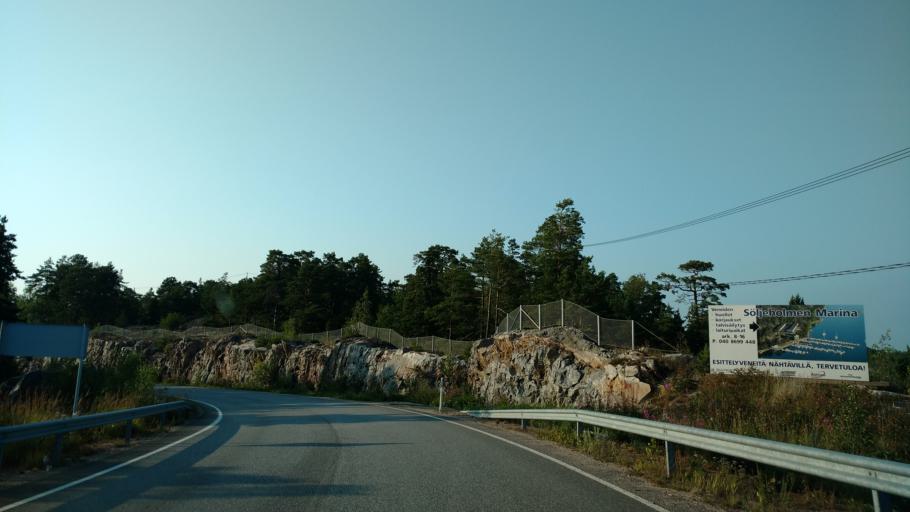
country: FI
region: Varsinais-Suomi
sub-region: Aboland-Turunmaa
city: Dragsfjaerd
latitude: 59.9867
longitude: 22.4547
